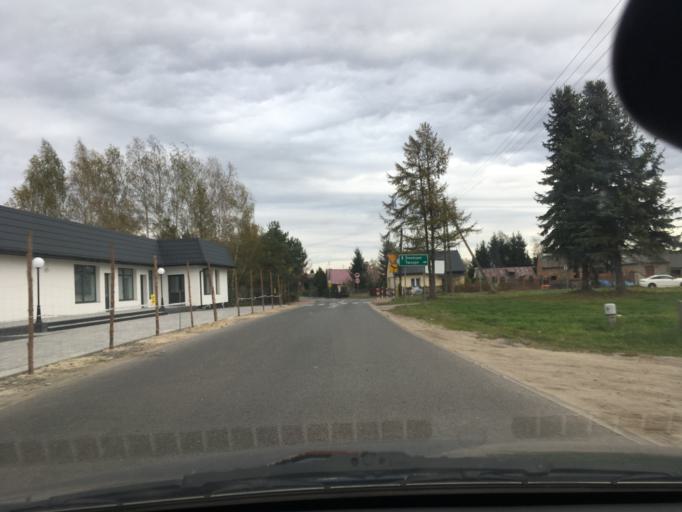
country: PL
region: Lodz Voivodeship
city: Zabia Wola
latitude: 52.0146
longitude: 20.7284
